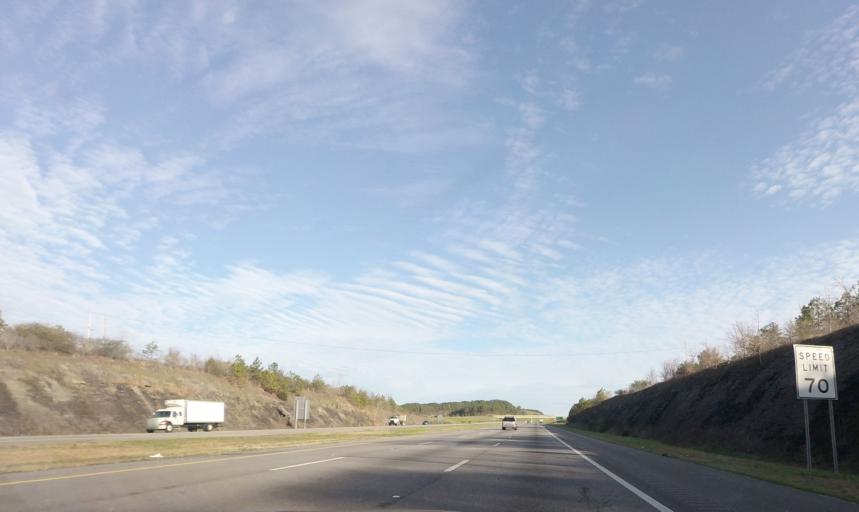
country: US
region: Alabama
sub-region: Walker County
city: Cordova
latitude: 33.7904
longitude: -87.2285
